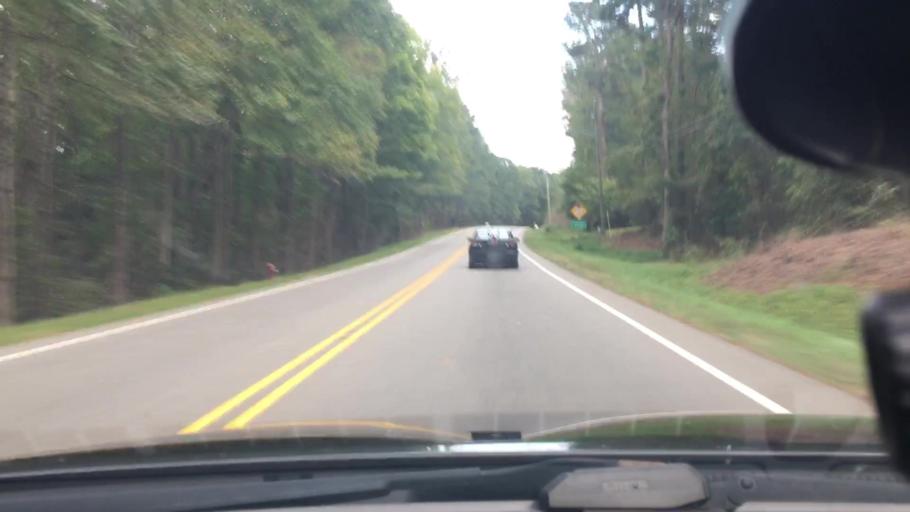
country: US
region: North Carolina
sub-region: Moore County
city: Carthage
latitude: 35.3596
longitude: -79.4359
